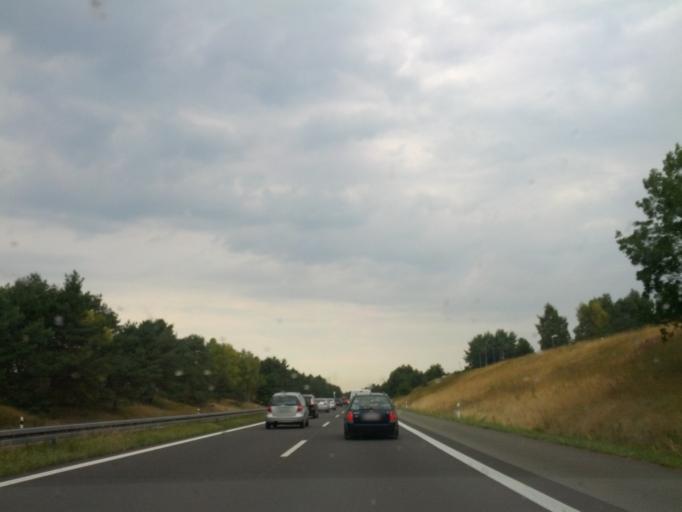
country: DE
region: Brandenburg
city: Walsleben
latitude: 52.9497
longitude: 12.6624
